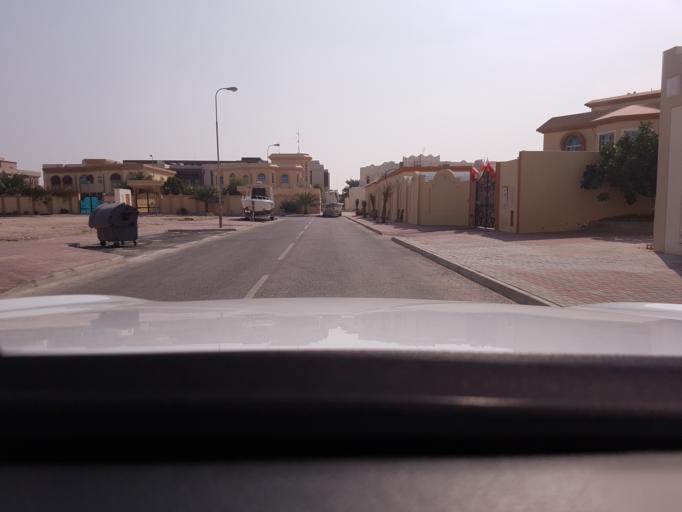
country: QA
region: Baladiyat ad Dawhah
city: Doha
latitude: 25.2339
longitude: 51.5598
